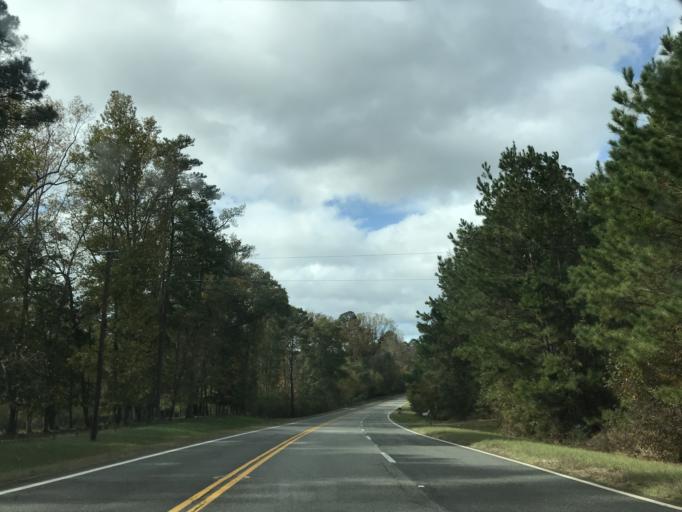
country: US
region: Georgia
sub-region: Jones County
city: Gray
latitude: 32.9726
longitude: -83.4987
